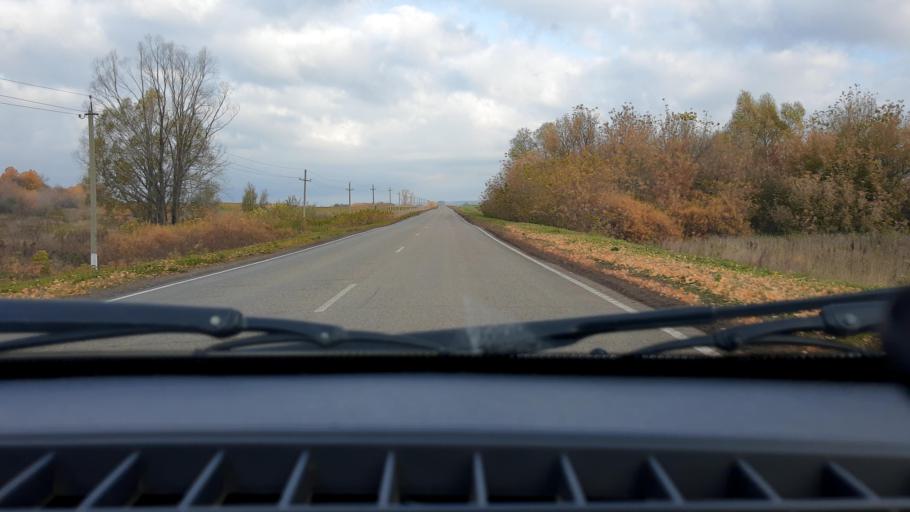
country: RU
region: Bashkortostan
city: Ulukulevo
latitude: 54.4010
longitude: 56.3776
